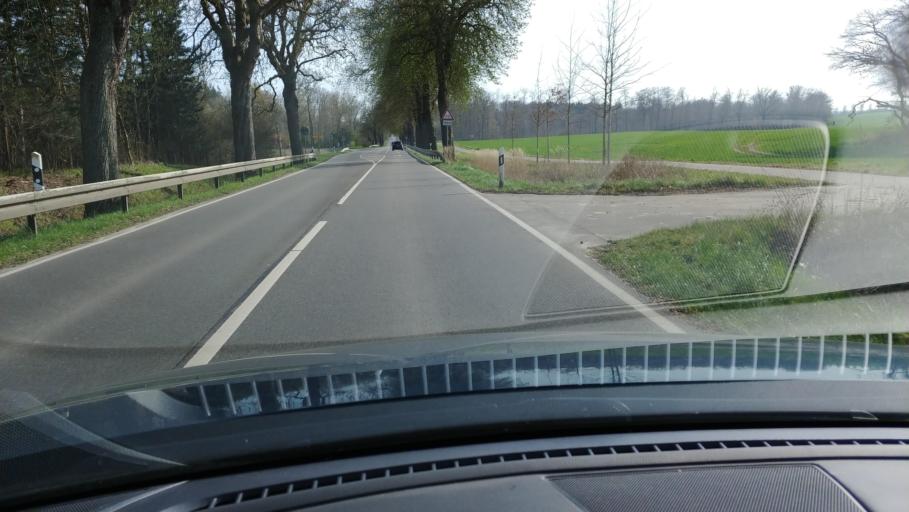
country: DE
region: Mecklenburg-Vorpommern
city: Lubstorf
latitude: 53.7394
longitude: 11.4074
